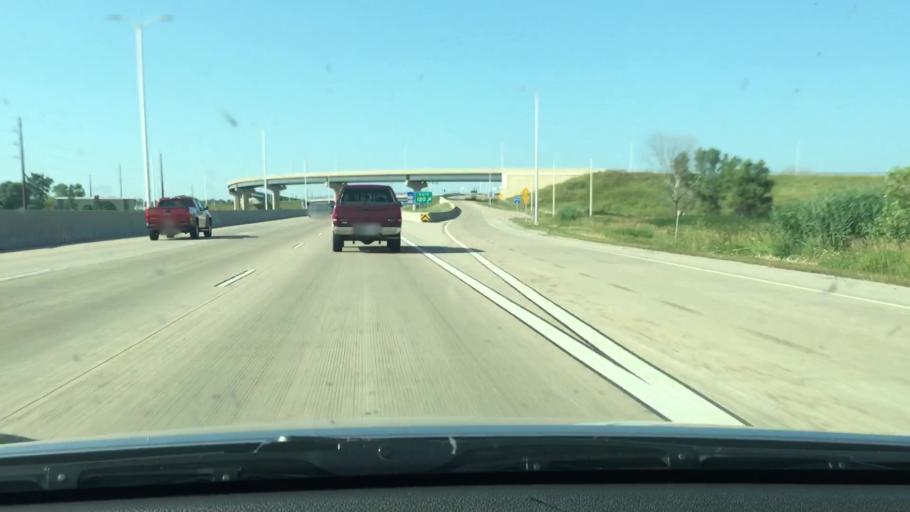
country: US
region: Wisconsin
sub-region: Winnebago County
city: Oshkosh
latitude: 44.0639
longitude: -88.5716
